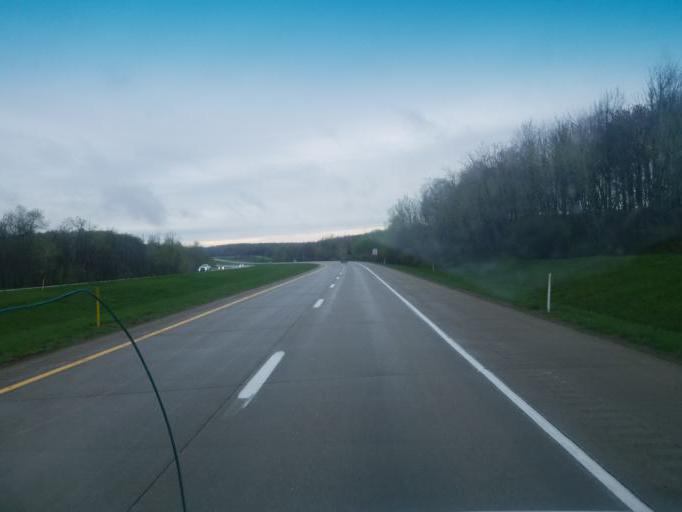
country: US
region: Pennsylvania
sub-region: Erie County
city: North East
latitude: 42.1441
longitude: -79.8334
